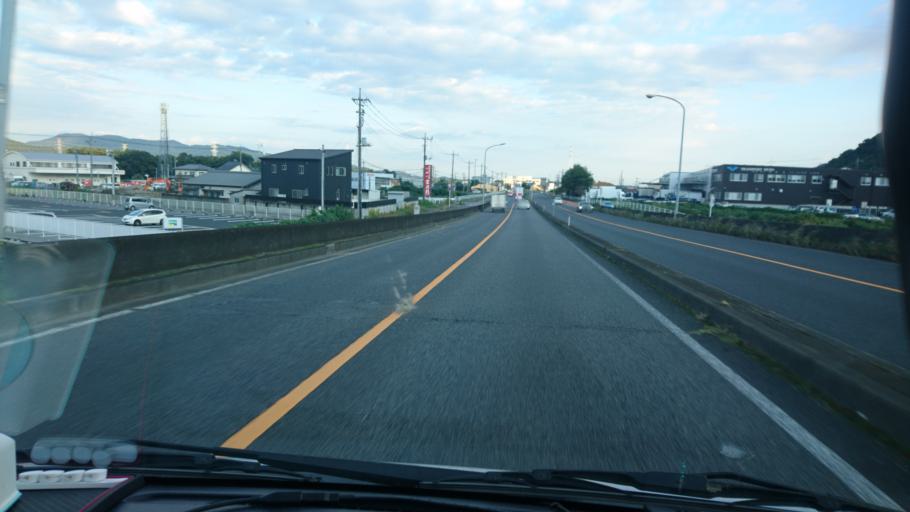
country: JP
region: Gunma
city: Kiryu
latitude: 36.3688
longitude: 139.3583
